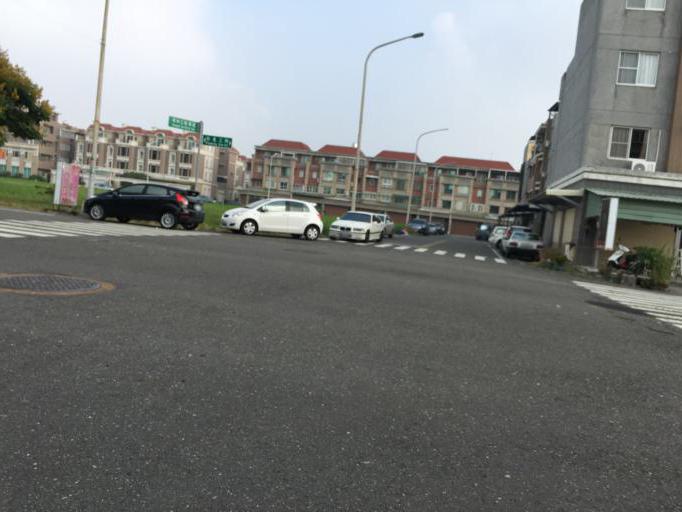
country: TW
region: Taiwan
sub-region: Chiayi
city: Taibao
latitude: 23.4557
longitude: 120.2858
